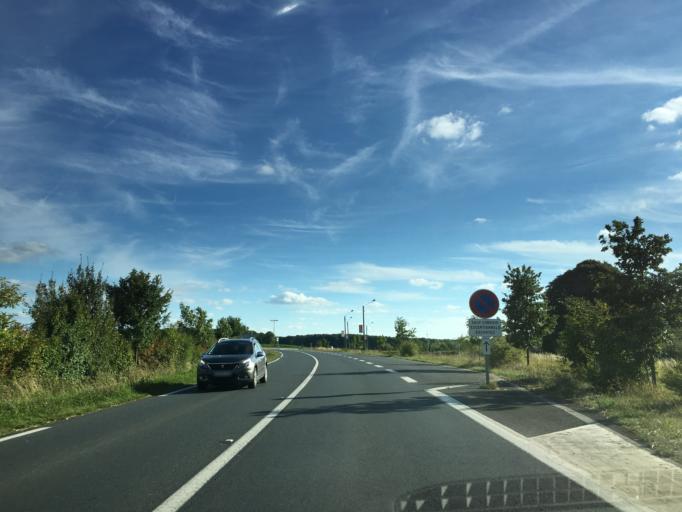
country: FR
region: Lower Normandy
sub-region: Departement du Calvados
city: Orbec
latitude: 48.8934
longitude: 0.4013
